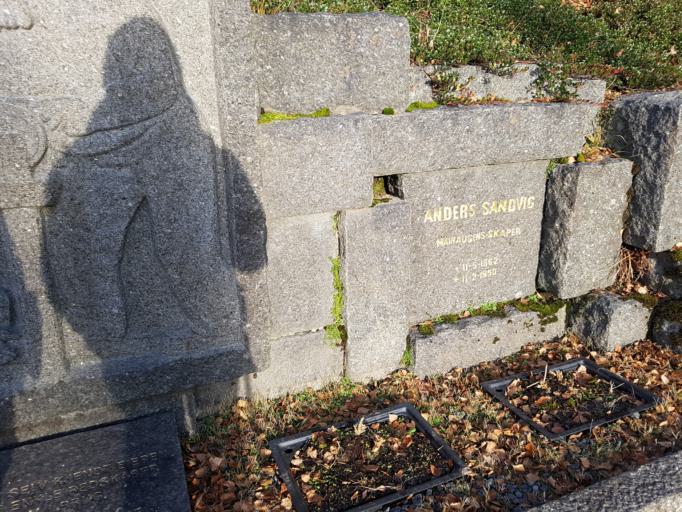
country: NO
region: Oppland
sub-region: Lillehammer
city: Lillehammer
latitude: 61.1109
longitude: 10.4769
